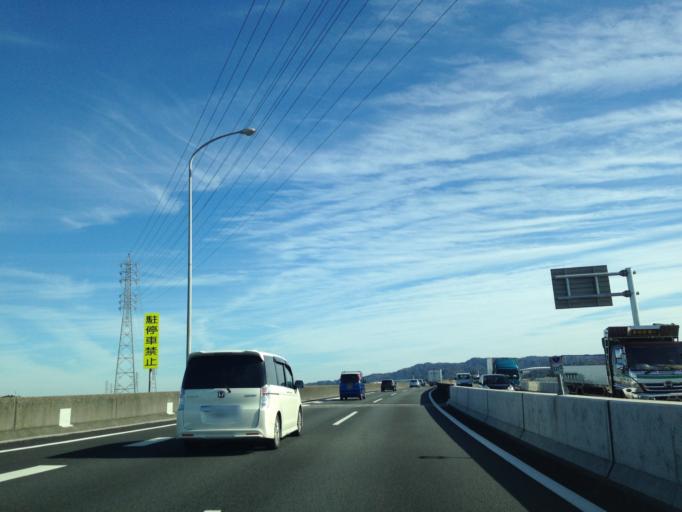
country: JP
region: Shizuoka
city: Fukuroi
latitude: 34.7580
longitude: 137.9274
